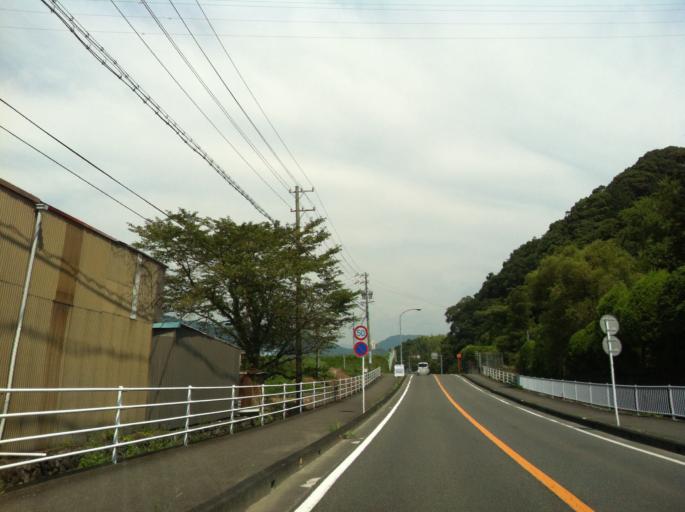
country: JP
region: Shizuoka
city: Shizuoka-shi
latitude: 35.0451
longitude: 138.3764
